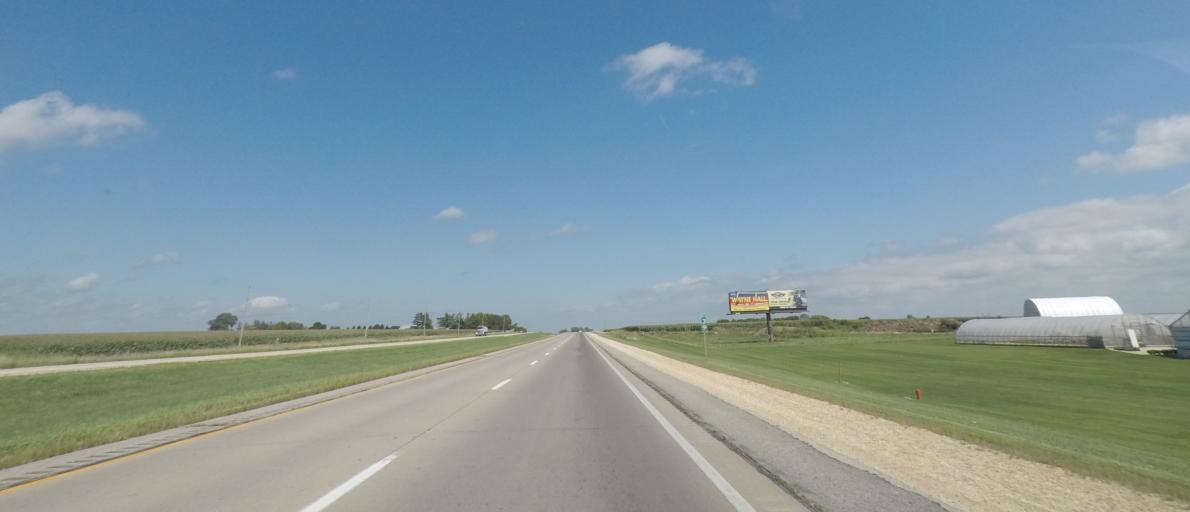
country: US
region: Iowa
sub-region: Linn County
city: Marion
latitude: 42.0381
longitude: -91.5283
